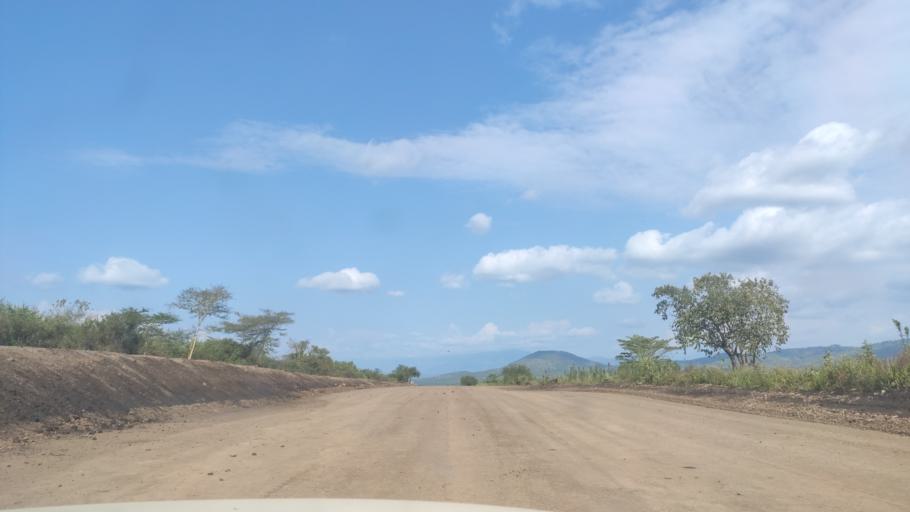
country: ET
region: Southern Nations, Nationalities, and People's Region
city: Felege Neway
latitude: 6.3979
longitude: 37.1145
